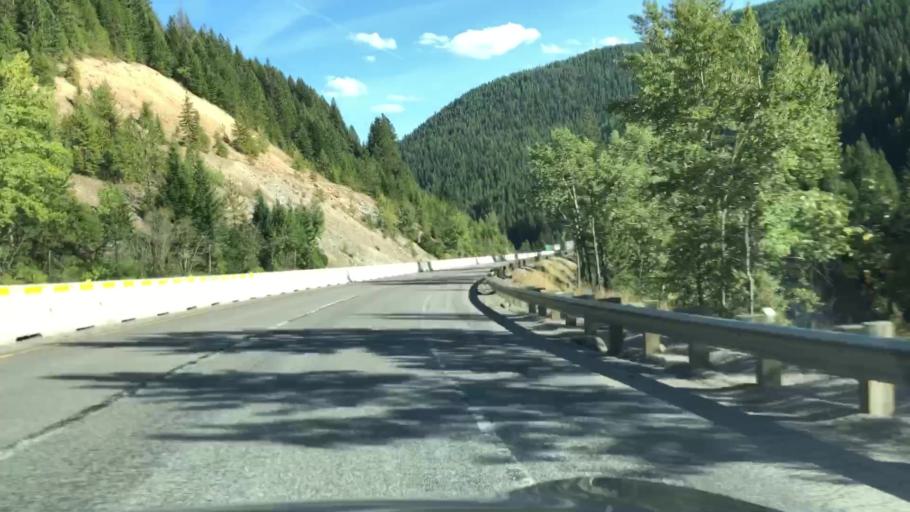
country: US
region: Montana
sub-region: Sanders County
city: Thompson Falls
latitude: 47.3980
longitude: -115.4578
